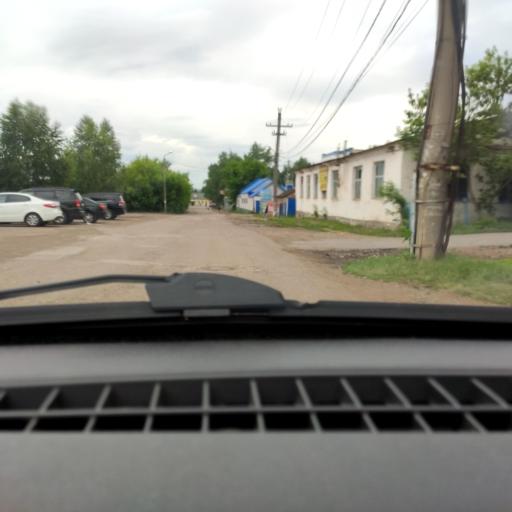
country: RU
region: Bashkortostan
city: Chishmy
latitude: 54.5884
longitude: 55.3892
